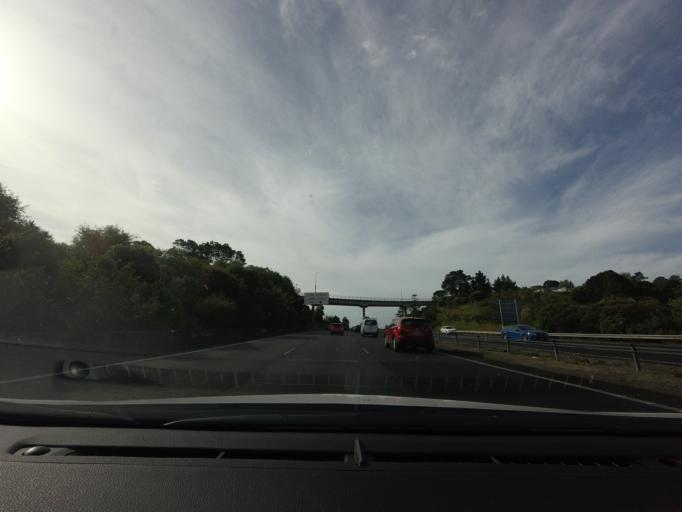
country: NZ
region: Auckland
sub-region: Auckland
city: Rothesay Bay
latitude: -36.7112
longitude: 174.7075
